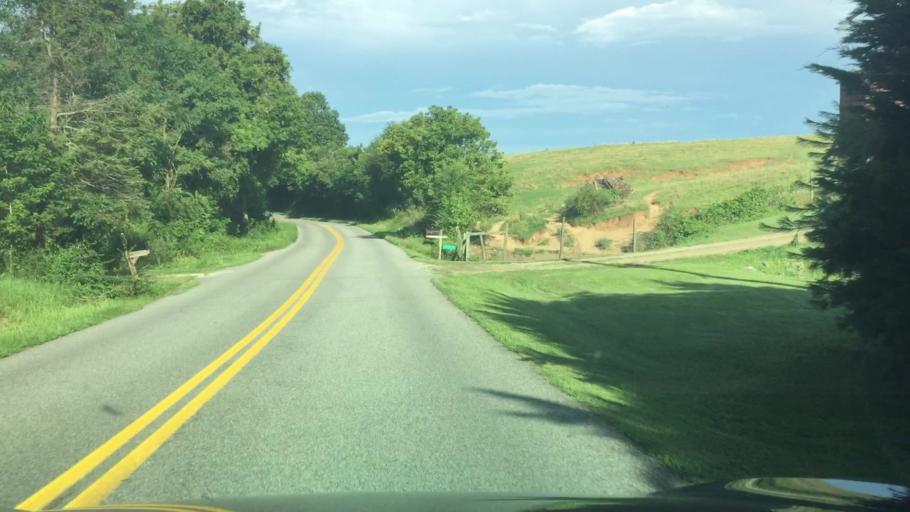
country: US
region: Virginia
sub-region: Wythe County
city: Wytheville
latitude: 36.9384
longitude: -80.9566
